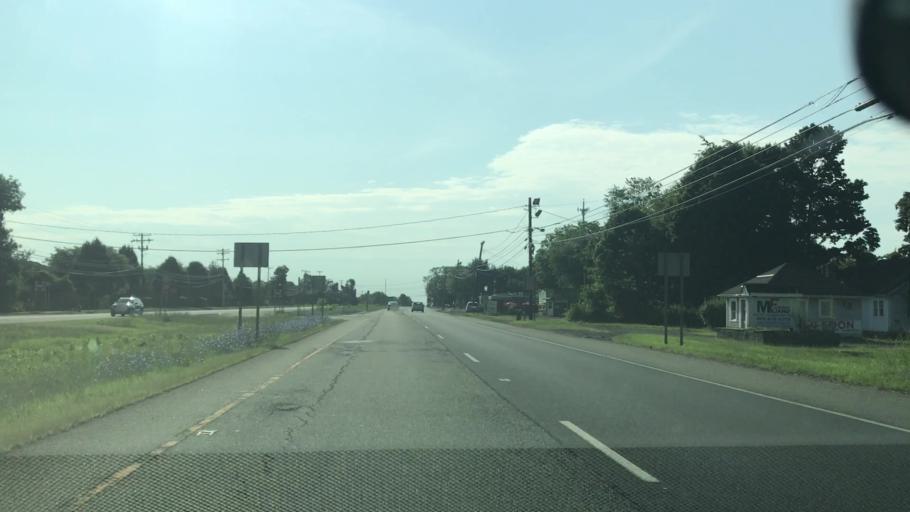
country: US
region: New Jersey
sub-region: Somerset County
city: Bridgewater
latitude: 40.6077
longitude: -74.7063
